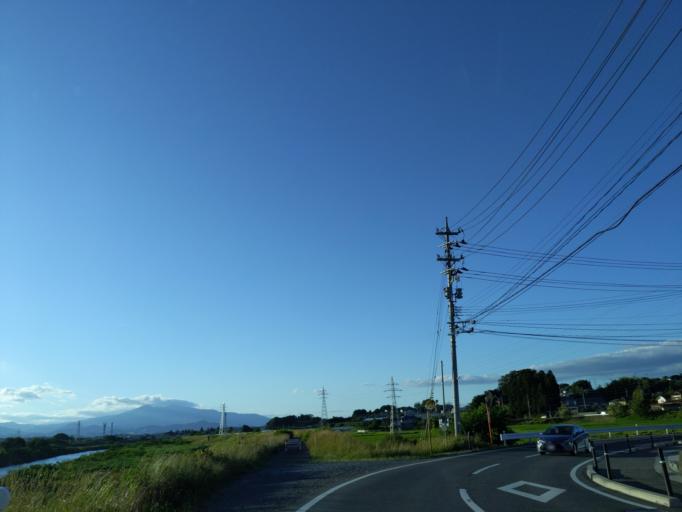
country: JP
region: Fukushima
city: Koriyama
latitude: 37.3963
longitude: 140.4116
